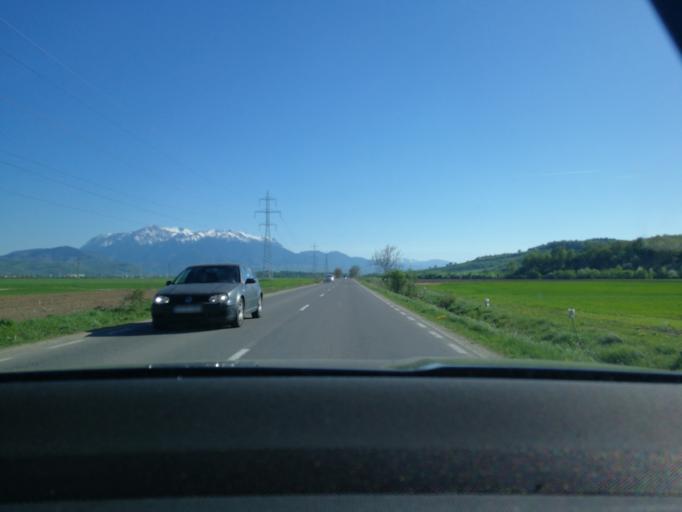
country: RO
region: Brasov
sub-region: Comuna Vulcan
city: Vulcan
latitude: 45.6198
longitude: 25.4250
